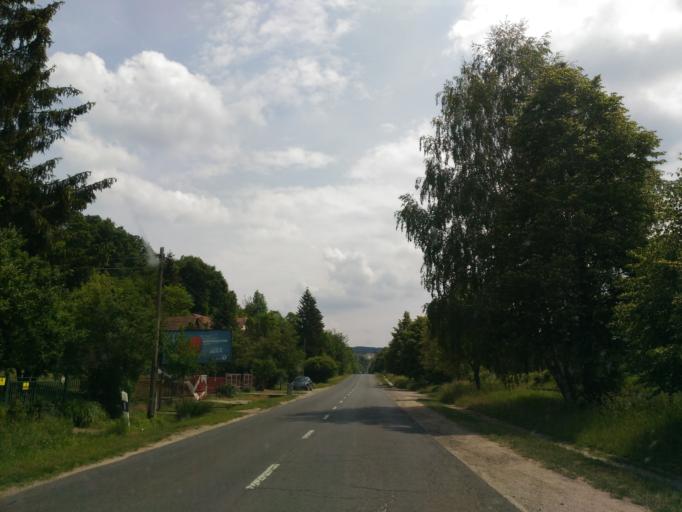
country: HU
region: Baranya
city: Komlo
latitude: 46.2051
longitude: 18.2487
